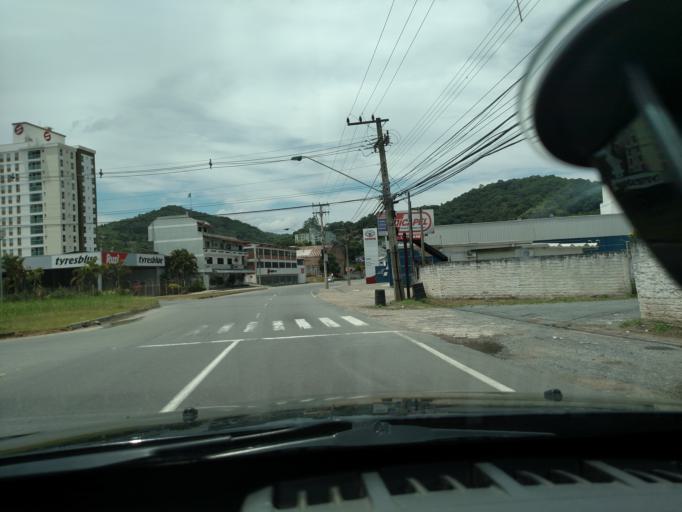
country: BR
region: Santa Catarina
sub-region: Blumenau
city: Blumenau
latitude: -26.8935
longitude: -49.0638
